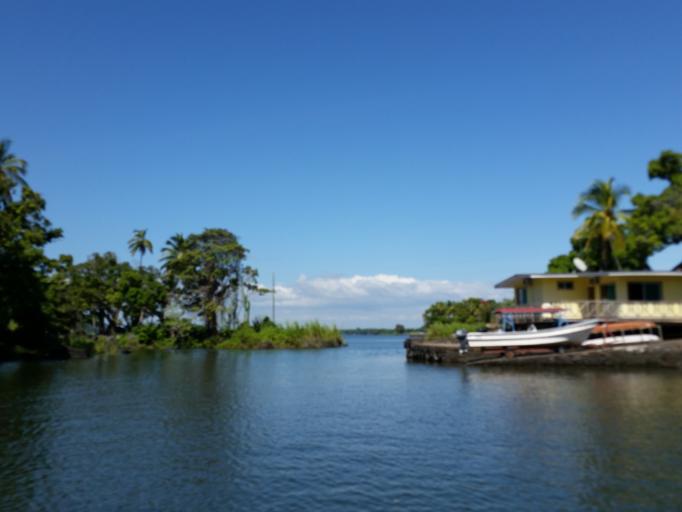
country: NI
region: Granada
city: Granada
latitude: 11.8725
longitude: -85.9038
